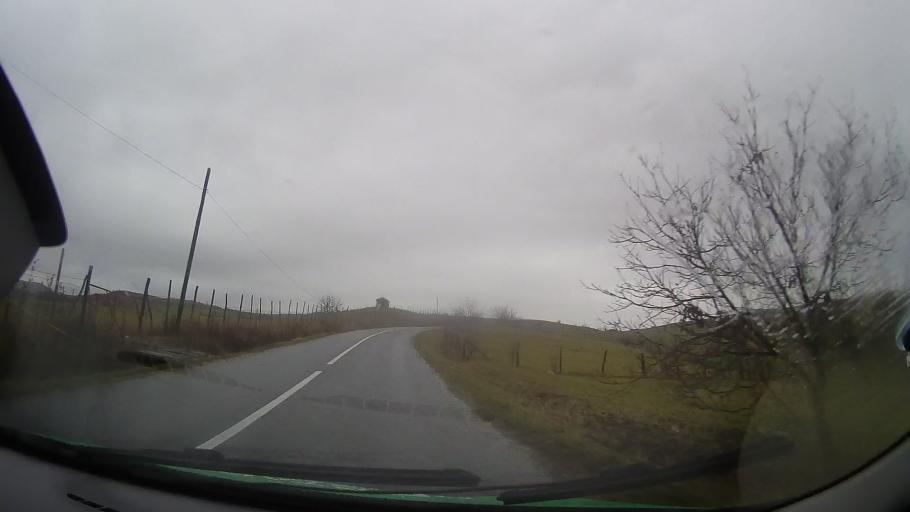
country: RO
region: Bistrita-Nasaud
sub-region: Comuna Monor
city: Monor
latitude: 46.9548
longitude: 24.6769
